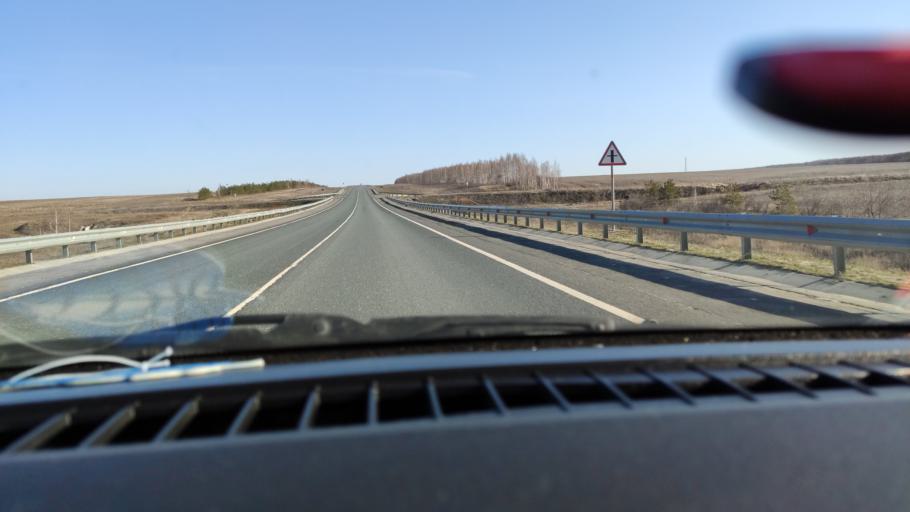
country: RU
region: Samara
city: Syzran'
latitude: 52.8869
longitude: 48.2932
